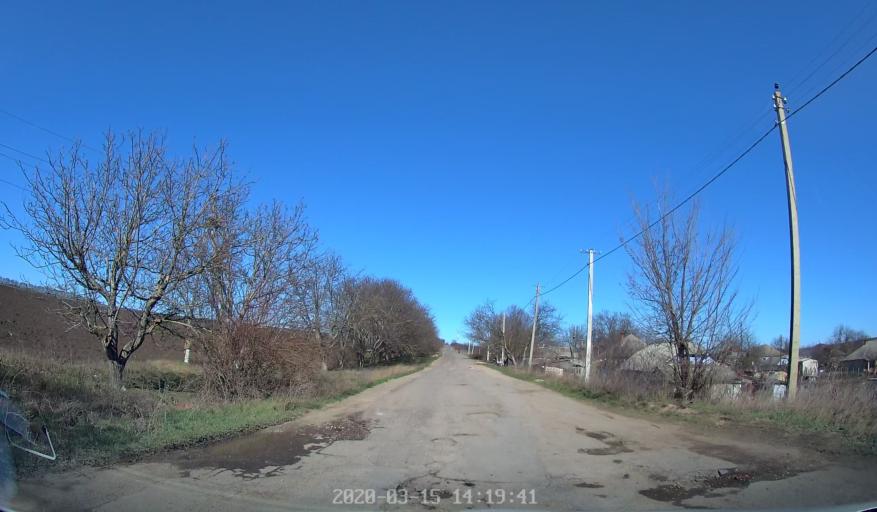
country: MD
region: Orhei
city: Orhei
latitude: 47.3058
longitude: 28.9173
